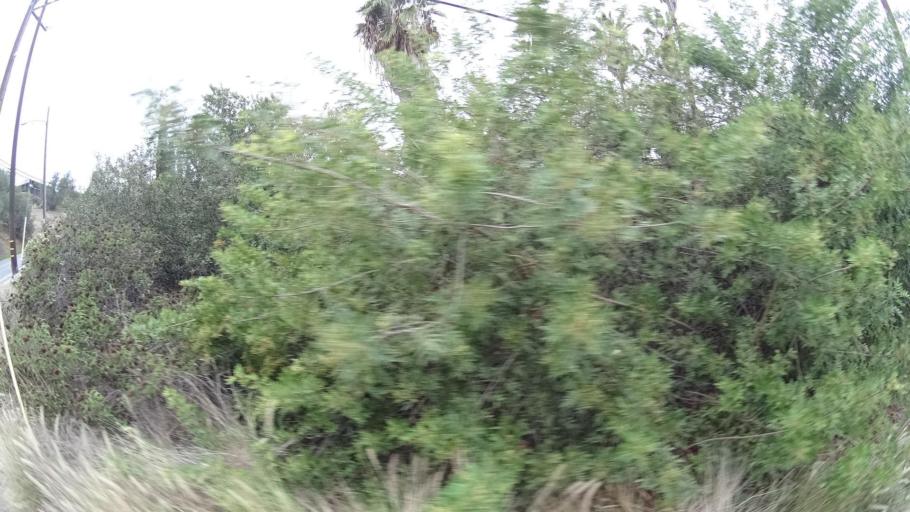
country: US
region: California
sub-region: San Diego County
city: Spring Valley
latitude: 32.7338
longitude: -116.9994
